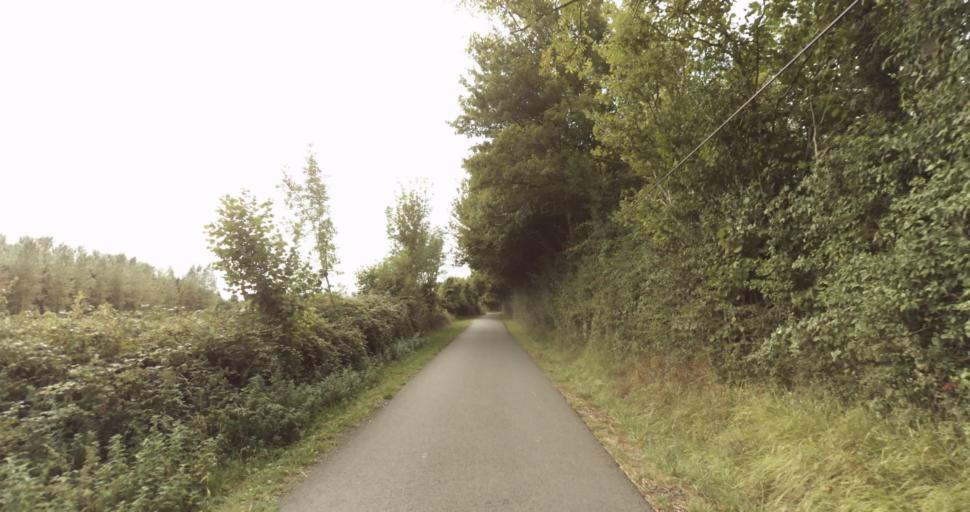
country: FR
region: Lower Normandy
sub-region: Departement de l'Orne
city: Gace
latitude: 48.7757
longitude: 0.3536
